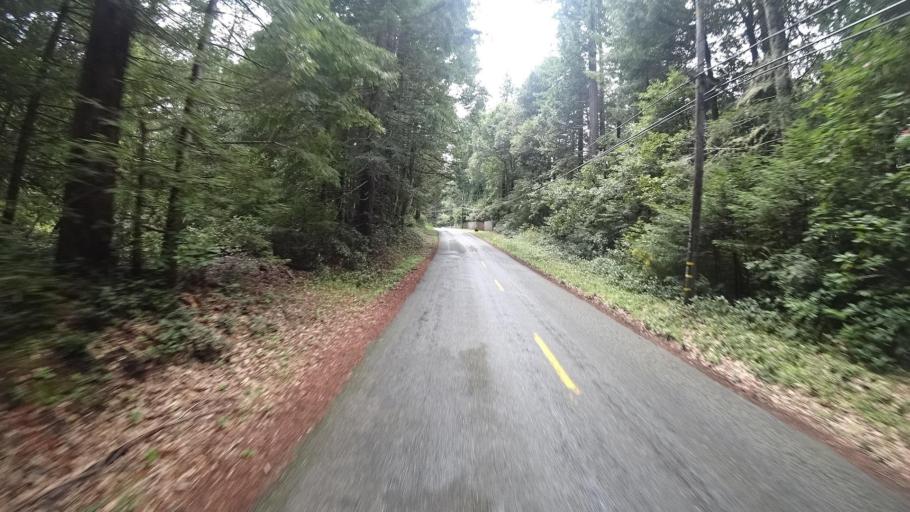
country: US
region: California
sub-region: Humboldt County
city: Bayside
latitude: 40.7725
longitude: -124.0014
